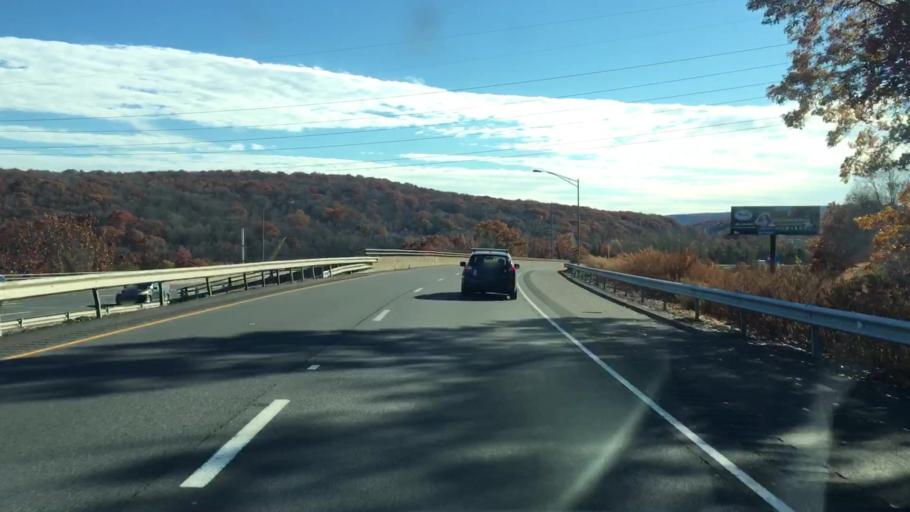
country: US
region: Connecticut
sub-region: New Haven County
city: Waterbury
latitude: 41.5256
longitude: -73.0452
